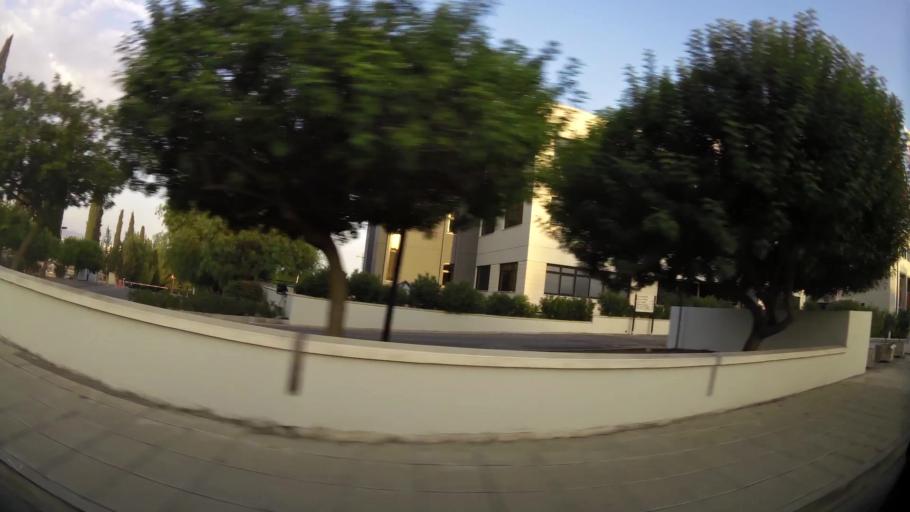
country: CY
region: Lefkosia
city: Nicosia
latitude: 35.1667
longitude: 33.3141
